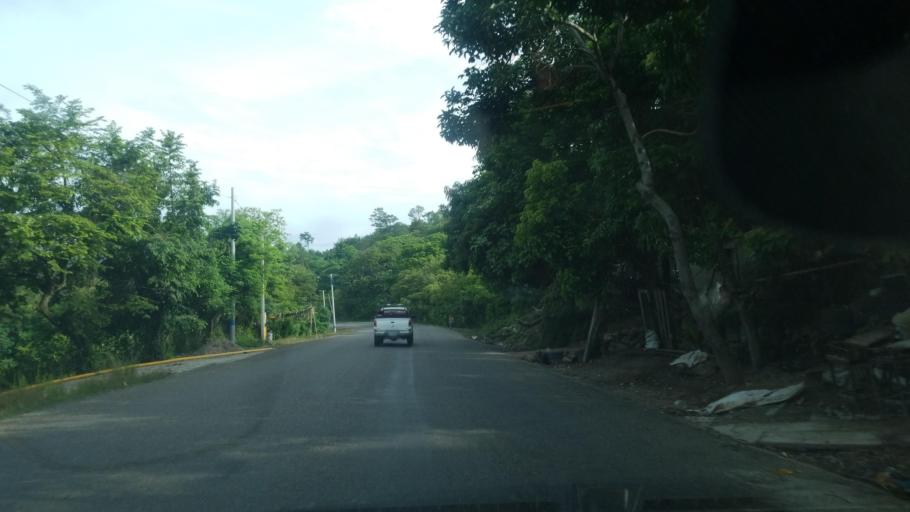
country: HN
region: Santa Barbara
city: Trinidad
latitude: 15.1657
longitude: -88.2607
